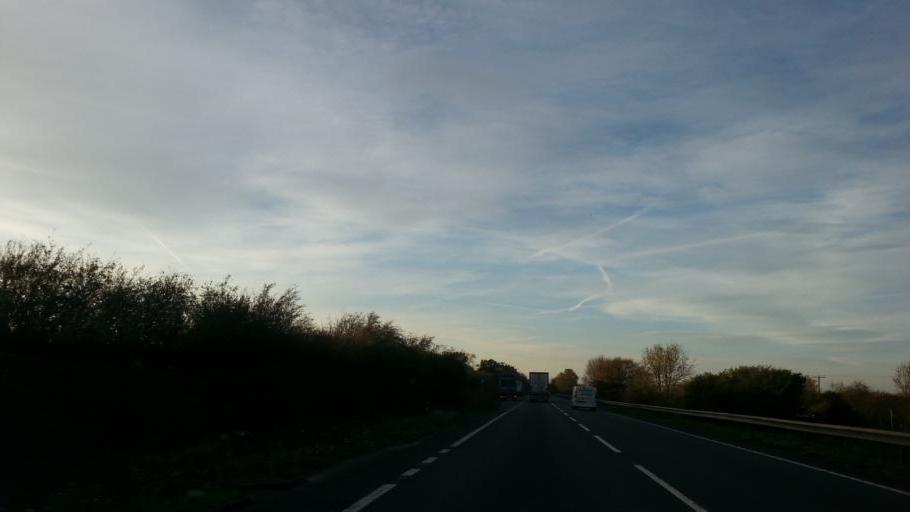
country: GB
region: England
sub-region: District of Rutland
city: Tickencote
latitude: 52.6950
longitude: -0.5684
